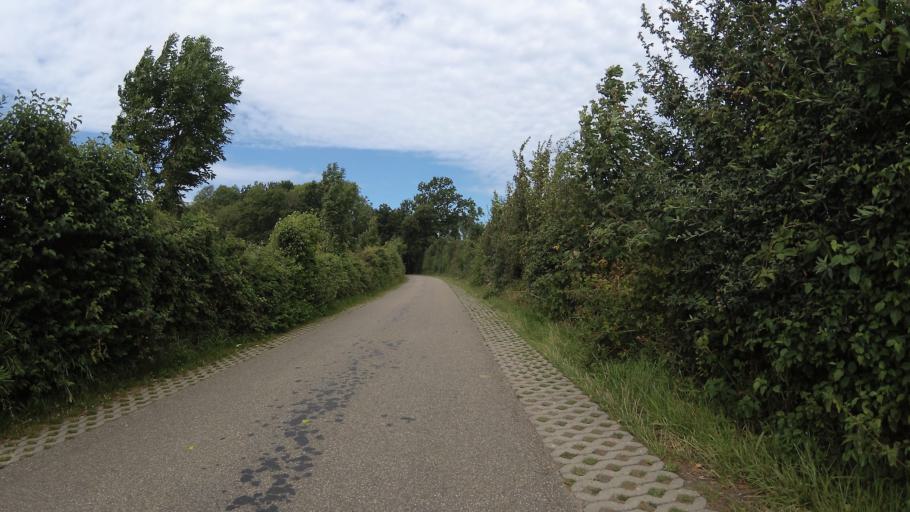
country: NL
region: Zeeland
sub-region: Gemeente Middelburg
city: Middelburg
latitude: 51.5754
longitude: 3.5594
